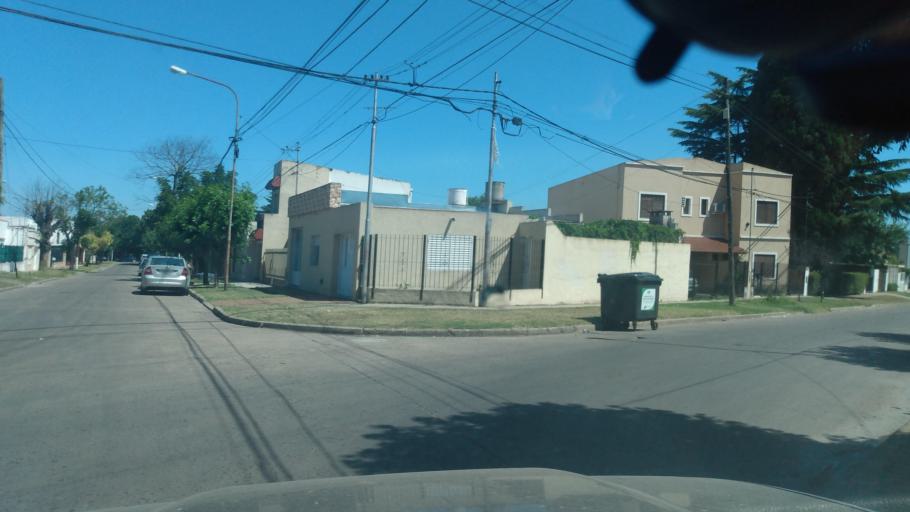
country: AR
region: Buenos Aires
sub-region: Partido de Lujan
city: Lujan
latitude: -34.5609
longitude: -59.1024
